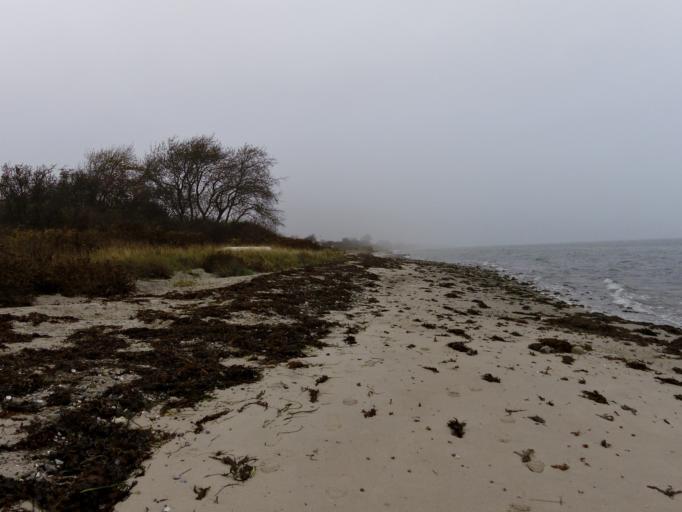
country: DK
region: Central Jutland
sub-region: Odder Kommune
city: Odder
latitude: 55.9384
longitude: 10.2604
